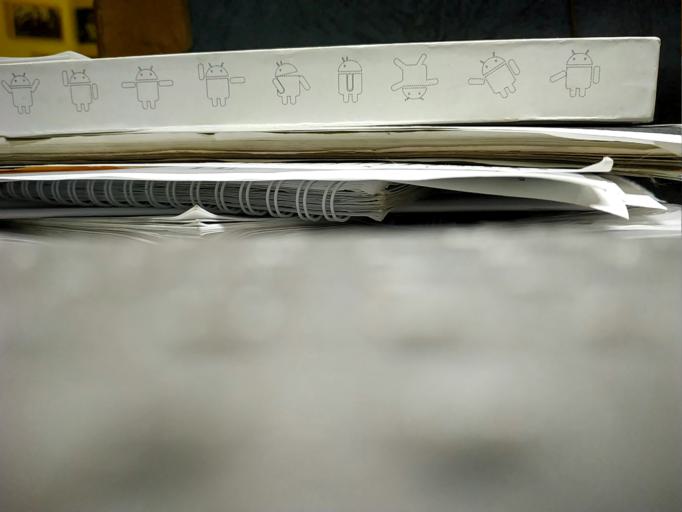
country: EE
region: Ida-Virumaa
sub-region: Narva linn
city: Narva
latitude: 59.4711
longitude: 28.2022
